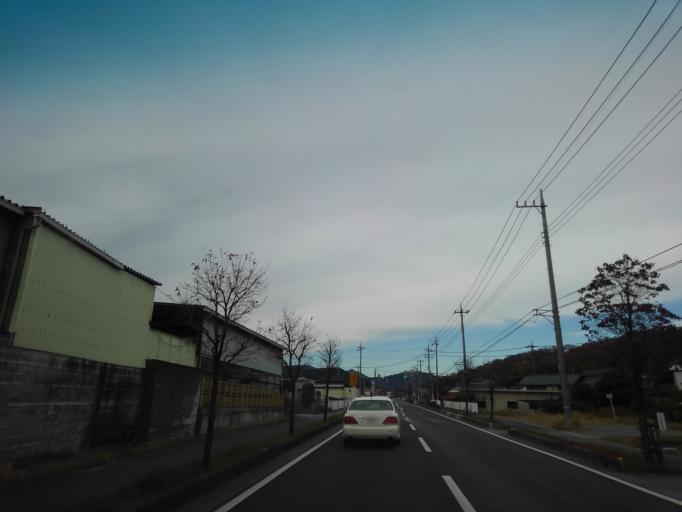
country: JP
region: Saitama
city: Morohongo
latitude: 35.9597
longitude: 139.3094
